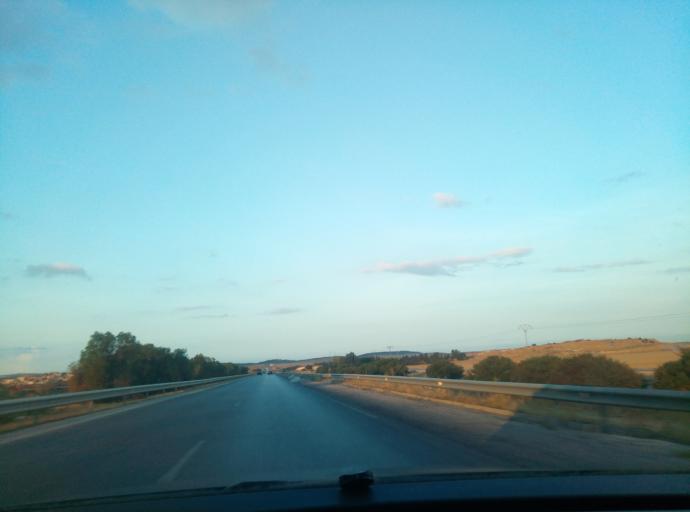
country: TN
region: Tunis
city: Oued Lill
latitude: 36.7354
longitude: 10.0204
